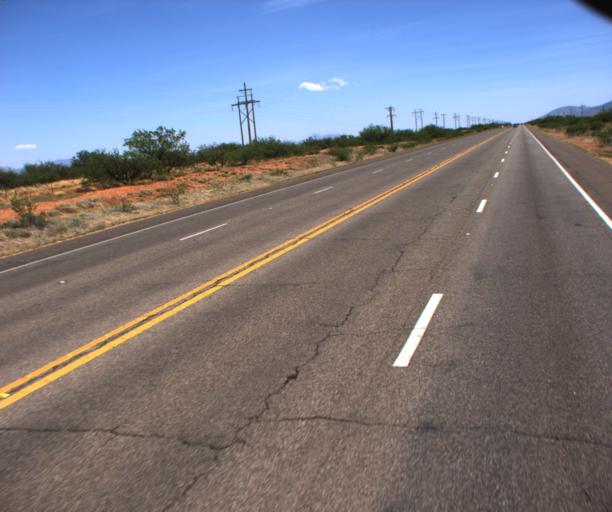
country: US
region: Arizona
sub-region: Cochise County
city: Huachuca City
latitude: 31.6071
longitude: -110.3305
